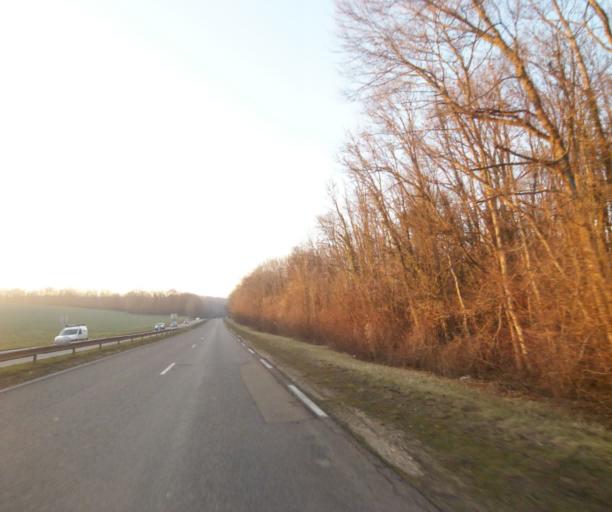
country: FR
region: Lorraine
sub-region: Departement de la Meuse
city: Ancerville
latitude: 48.6095
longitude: 5.0118
